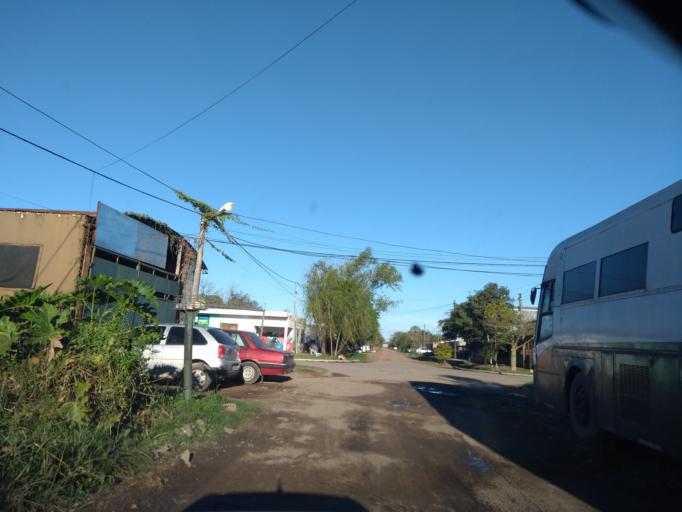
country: AR
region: Chaco
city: Barranqueras
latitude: -27.4898
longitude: -58.9406
